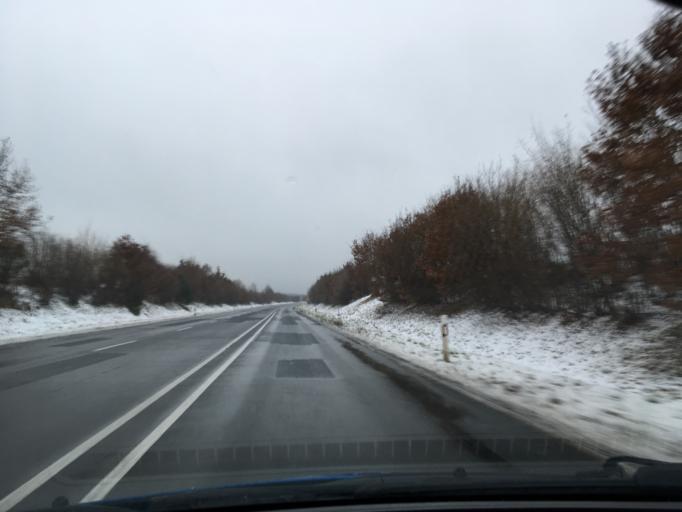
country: DE
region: Lower Saxony
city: Wrestedt
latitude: 52.9236
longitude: 10.5387
